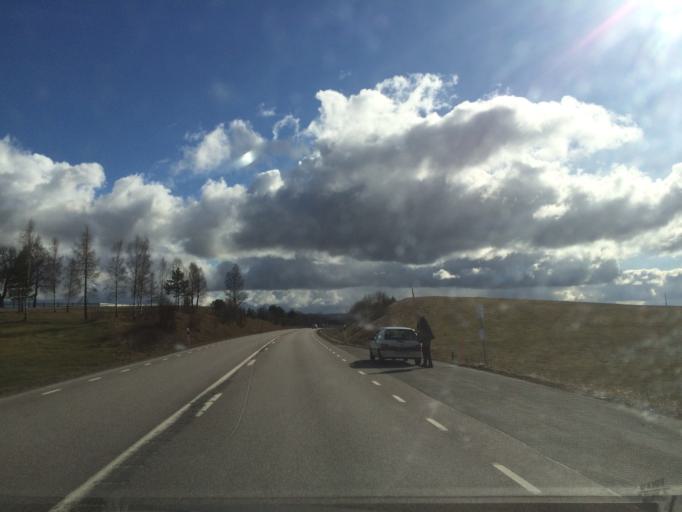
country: SE
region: Vaestra Goetaland
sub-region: Skara Kommun
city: Skara
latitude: 58.2843
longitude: 13.4836
